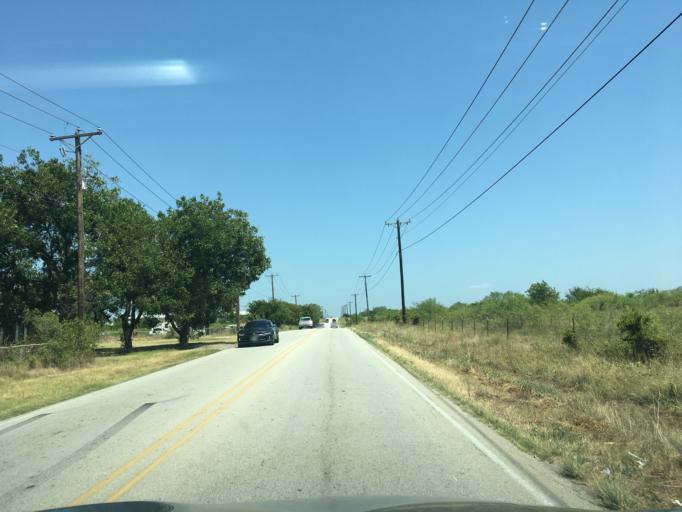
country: US
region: Texas
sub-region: Tarrant County
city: Crowley
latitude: 32.6141
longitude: -97.3427
